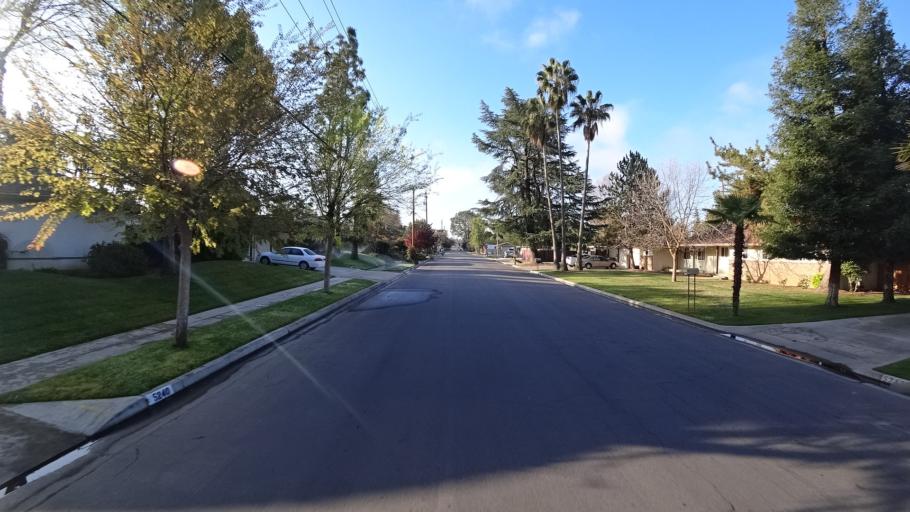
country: US
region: California
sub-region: Fresno County
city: Fresno
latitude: 36.8129
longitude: -119.7949
